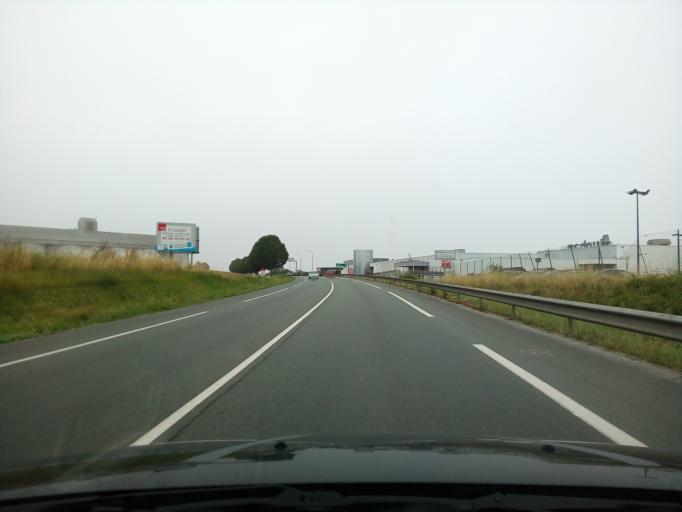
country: FR
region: Poitou-Charentes
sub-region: Departement de la Charente
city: Saint-Brice
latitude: 45.6828
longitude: -0.3033
